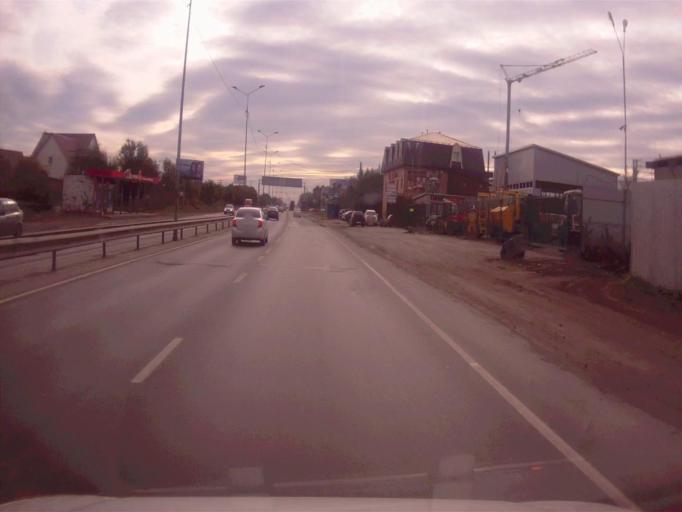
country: RU
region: Chelyabinsk
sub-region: Gorod Chelyabinsk
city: Chelyabinsk
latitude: 55.1115
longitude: 61.4103
